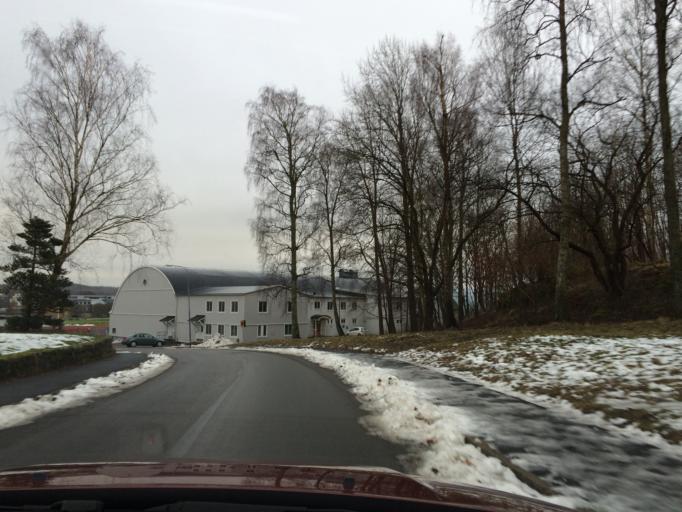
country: SE
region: Halland
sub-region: Kungsbacka Kommun
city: Kungsbacka
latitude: 57.4918
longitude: 12.0650
